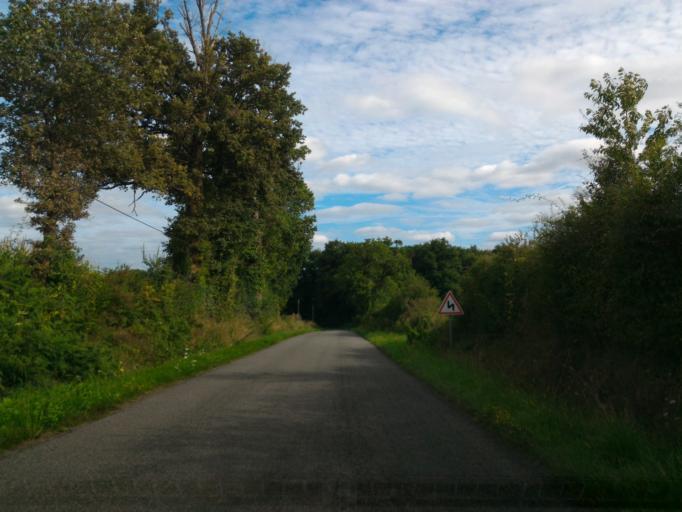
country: FR
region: Poitou-Charentes
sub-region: Departement de la Charente
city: Etagnac
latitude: 45.9456
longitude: 0.7936
